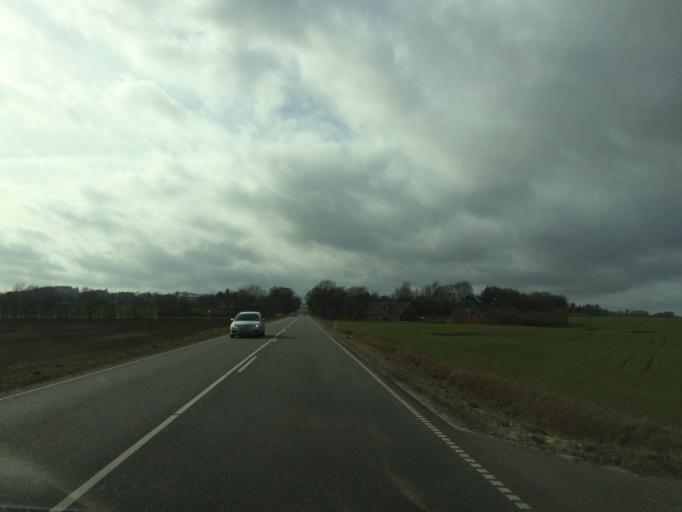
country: DK
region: Central Jutland
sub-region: Randers Kommune
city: Langa
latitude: 56.4931
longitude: 9.8516
